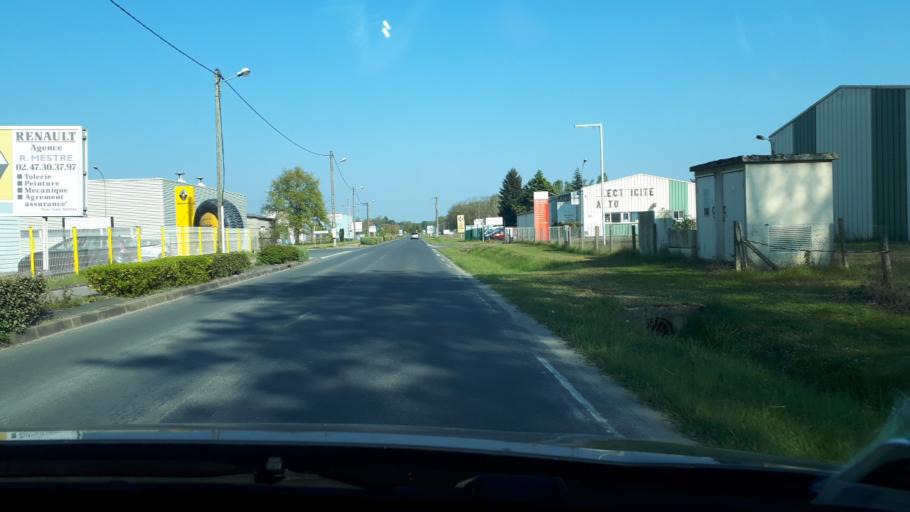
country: FR
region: Centre
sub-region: Departement d'Indre-et-Loire
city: Blere
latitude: 47.3242
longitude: 1.0135
